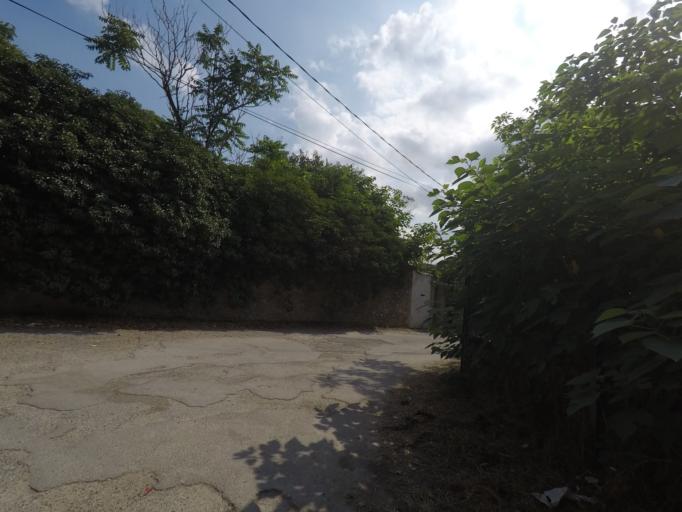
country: FR
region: Provence-Alpes-Cote d'Azur
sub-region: Departement des Bouches-du-Rhone
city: Marseille 10
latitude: 43.2655
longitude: 5.4177
